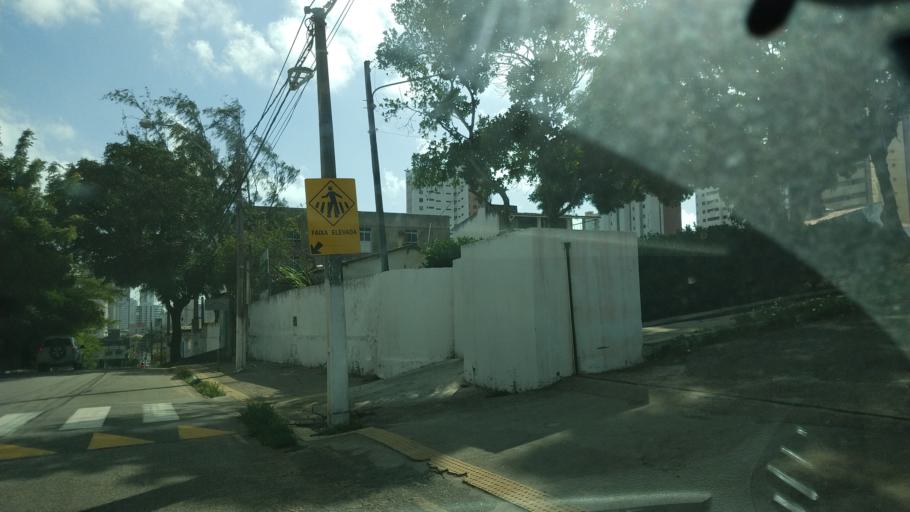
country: BR
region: Rio Grande do Norte
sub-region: Natal
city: Natal
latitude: -5.8013
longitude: -35.2042
